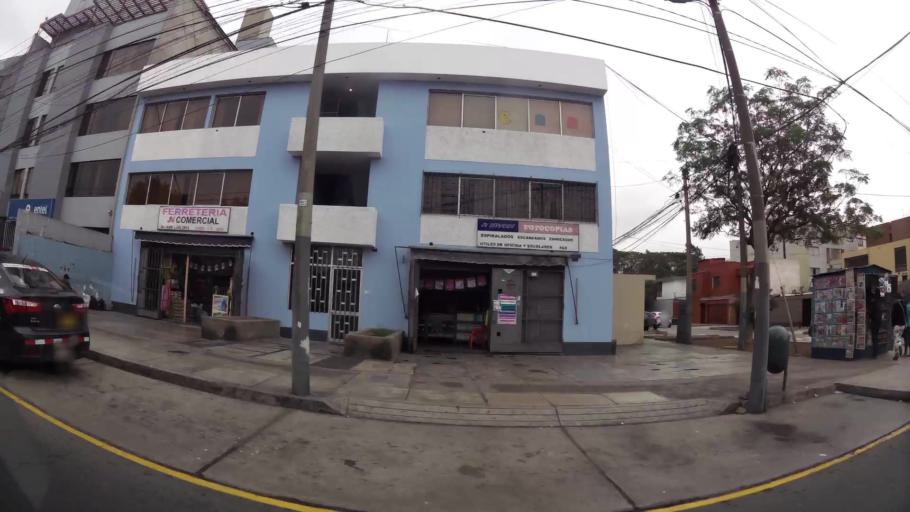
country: PE
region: Lima
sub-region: Lima
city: San Luis
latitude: -12.1020
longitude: -76.9942
